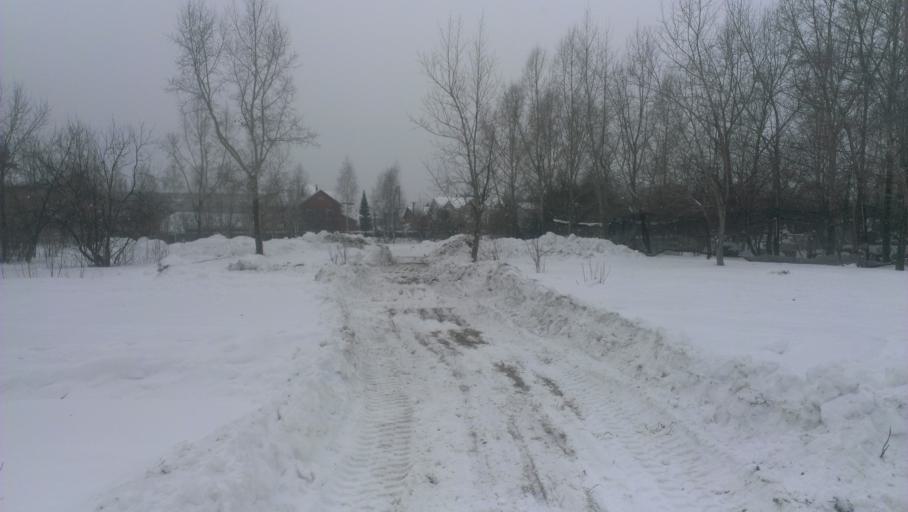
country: RU
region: Altai Krai
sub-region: Gorod Barnaulskiy
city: Barnaul
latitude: 53.3586
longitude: 83.6871
